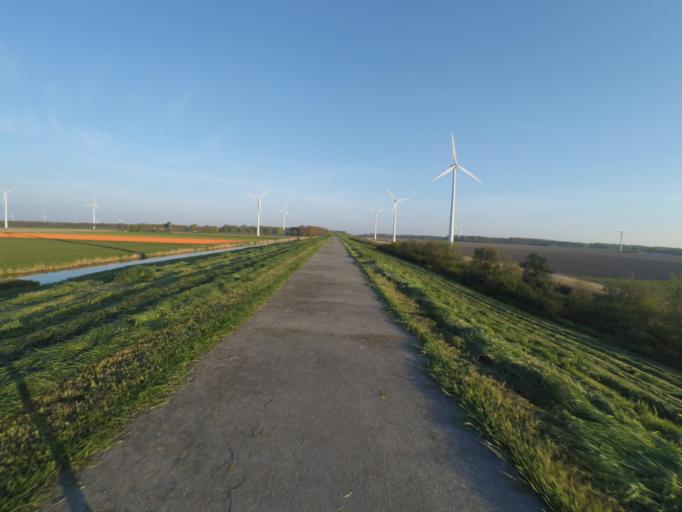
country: NL
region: Flevoland
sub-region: Gemeente Zeewolde
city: Zeewolde
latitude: 52.3952
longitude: 5.5147
